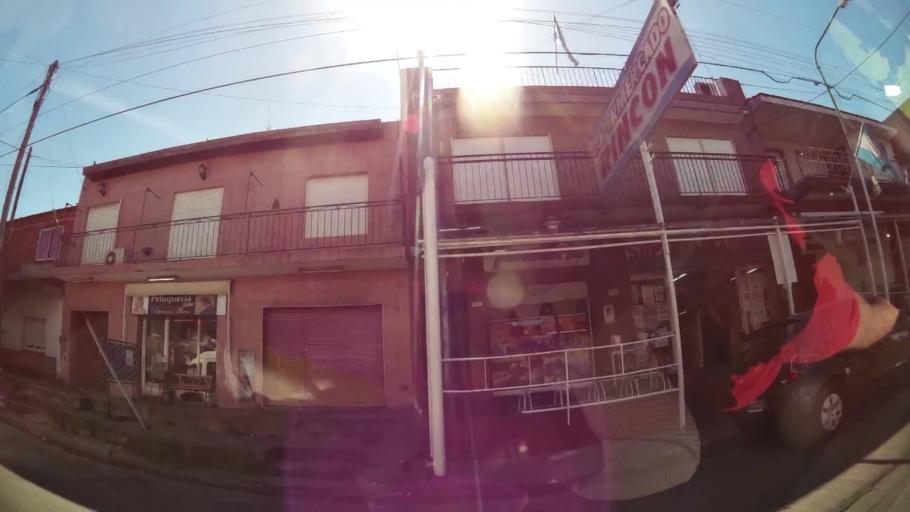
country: AR
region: Buenos Aires
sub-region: Partido de Tigre
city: Tigre
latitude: -34.4940
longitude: -58.6119
